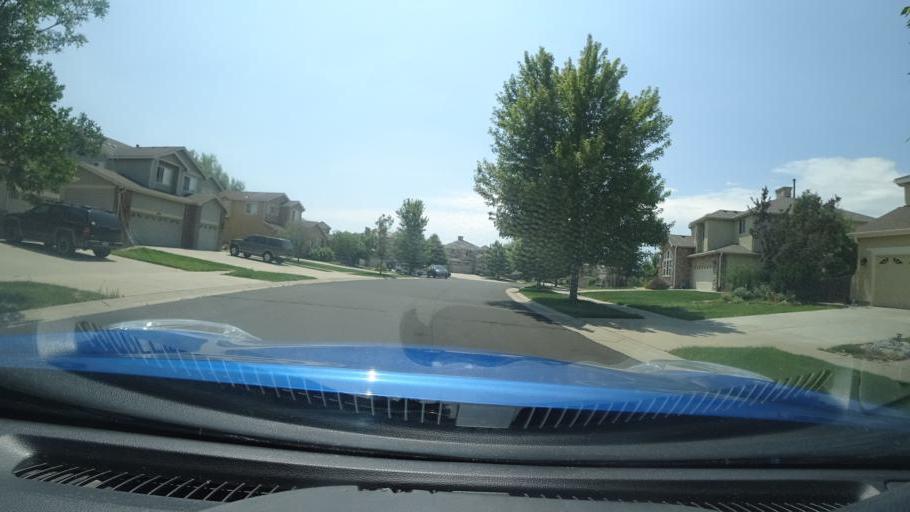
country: US
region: Colorado
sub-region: Adams County
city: Aurora
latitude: 39.6738
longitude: -104.7575
